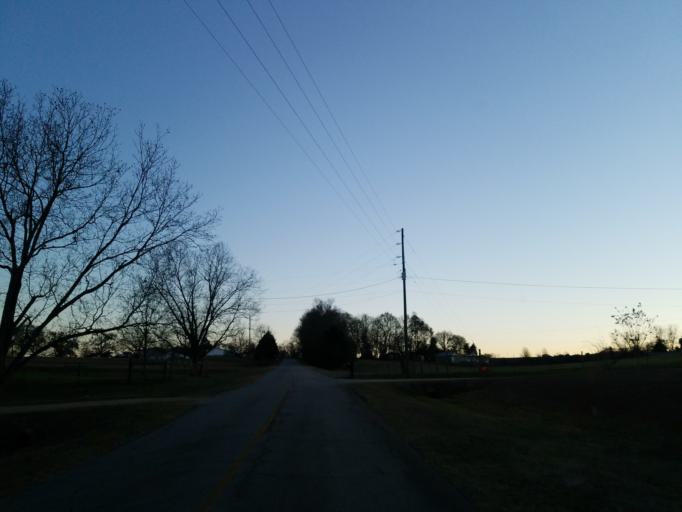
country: US
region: Georgia
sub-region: Monroe County
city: Forsyth
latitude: 32.9873
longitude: -83.8796
